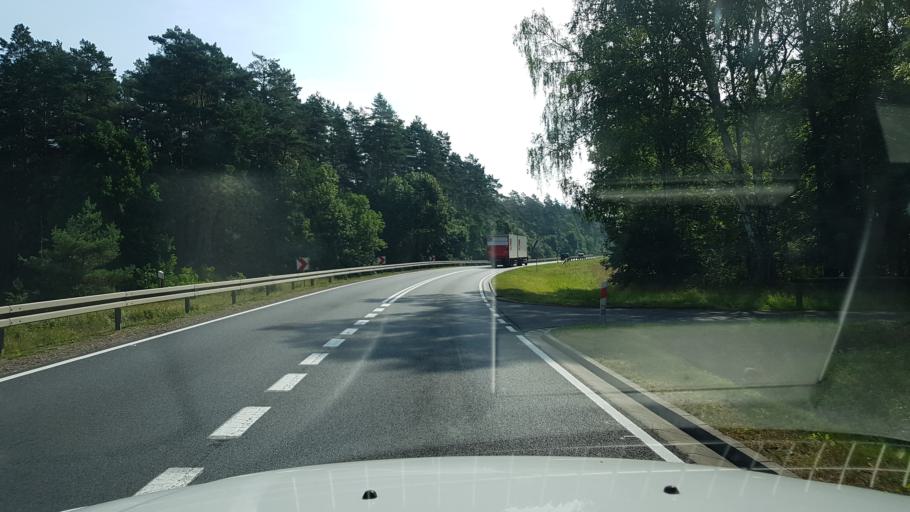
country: PL
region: West Pomeranian Voivodeship
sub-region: Powiat walecki
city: Miroslawiec
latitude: 53.3499
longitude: 16.1643
